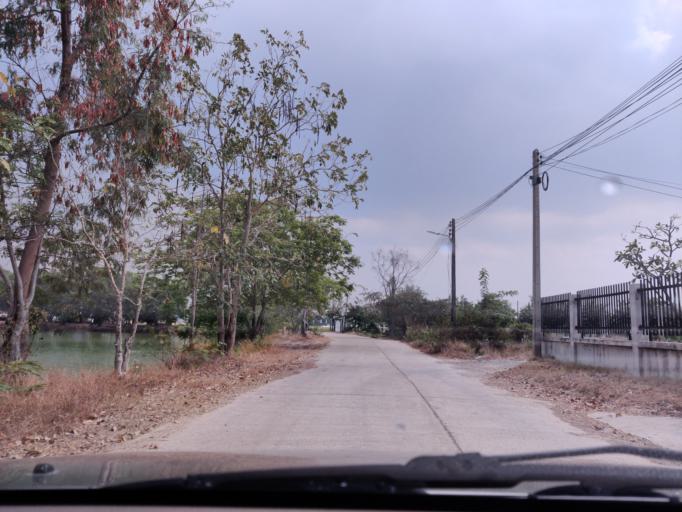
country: TH
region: Sisaket
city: Si Sa Ket
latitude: 15.1034
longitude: 104.3502
